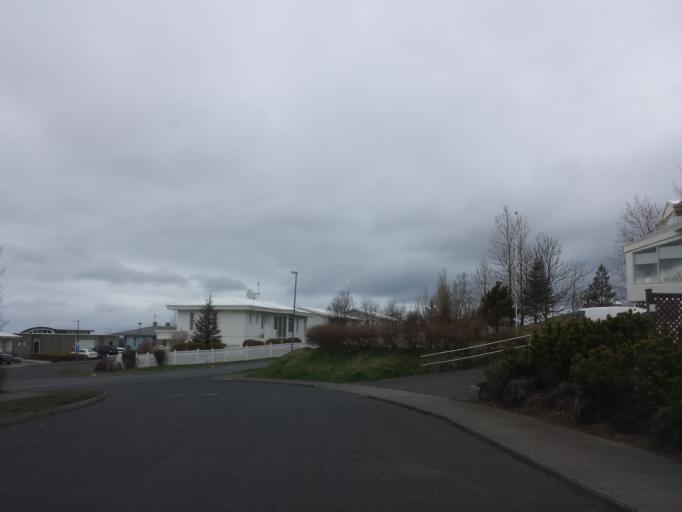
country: IS
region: Capital Region
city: Kopavogur
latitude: 64.0952
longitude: -21.8935
